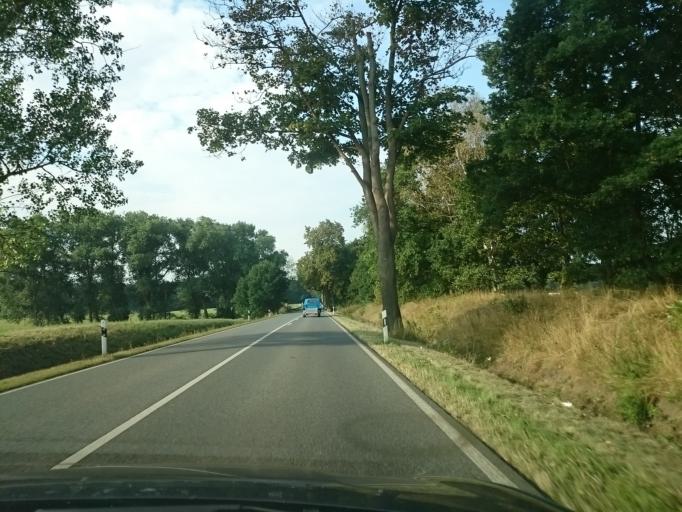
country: DE
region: Mecklenburg-Vorpommern
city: Demmin
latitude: 53.8710
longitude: 13.0167
